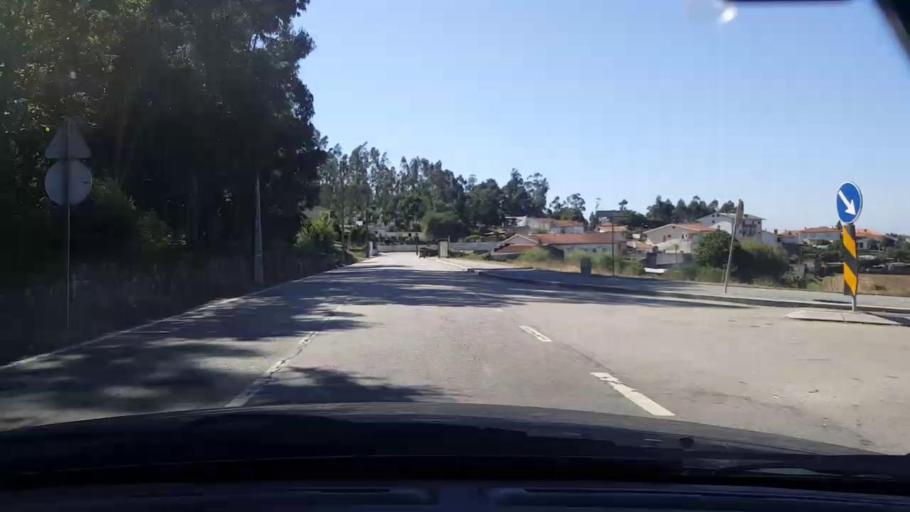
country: PT
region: Porto
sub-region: Vila do Conde
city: Arvore
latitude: 41.3424
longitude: -8.6581
